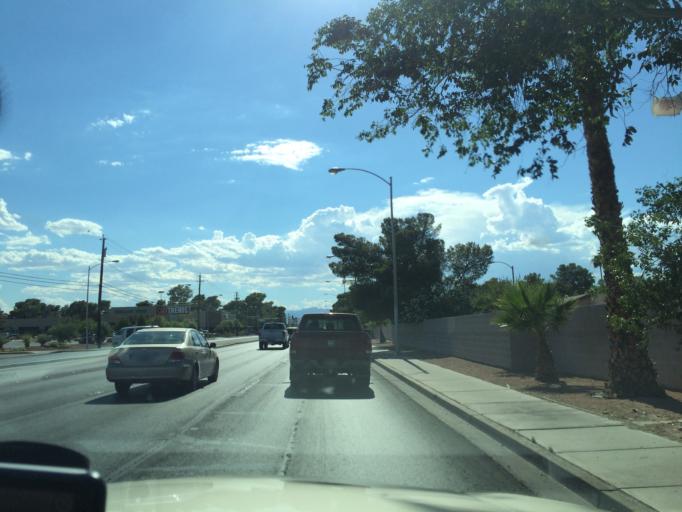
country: US
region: Nevada
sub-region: Clark County
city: Winchester
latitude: 36.1001
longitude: -115.1072
